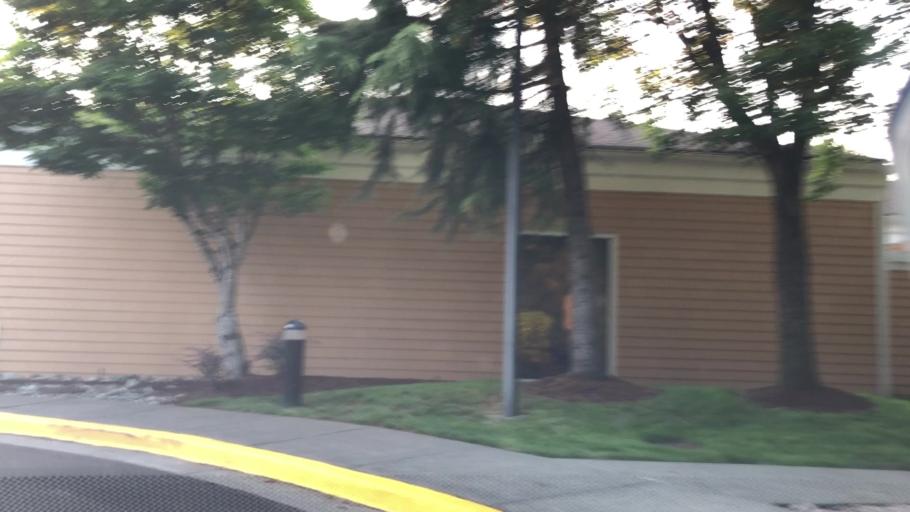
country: US
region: Washington
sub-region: King County
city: Redmond
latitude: 47.6350
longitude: -122.1456
